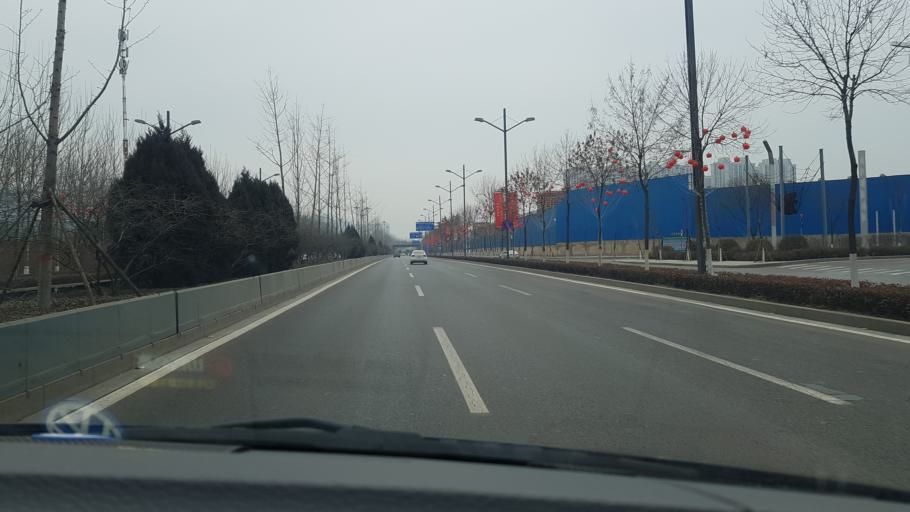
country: CN
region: Shanxi Sheng
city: Qianfeng
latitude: 37.8003
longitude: 112.5308
